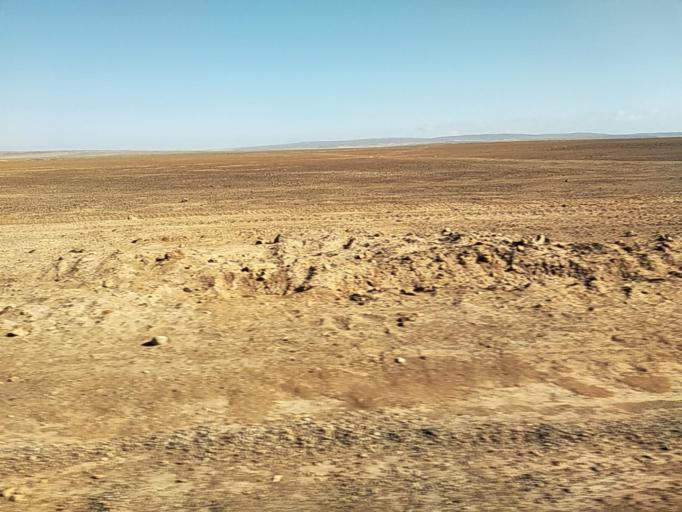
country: CL
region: Atacama
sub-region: Provincia de Copiapo
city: Copiapo
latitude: -27.3165
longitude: -70.8484
